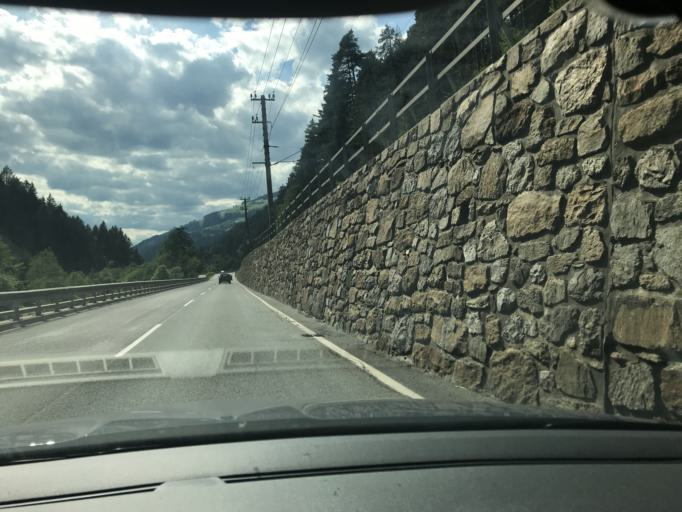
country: AT
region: Tyrol
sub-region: Politischer Bezirk Lienz
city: Leisach
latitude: 46.7855
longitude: 12.6883
